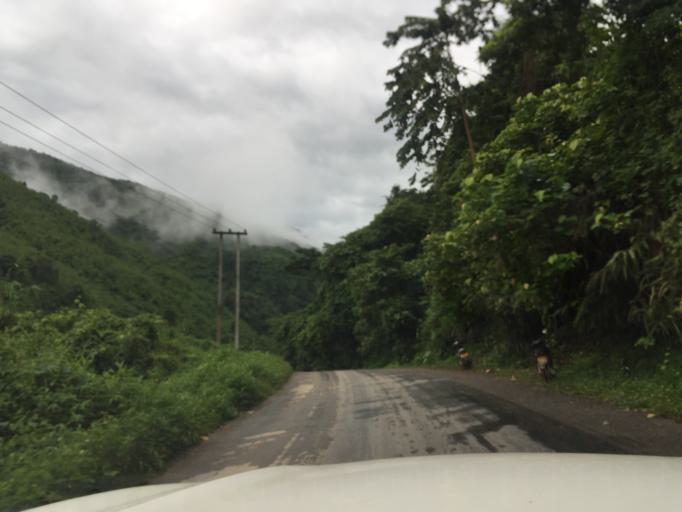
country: LA
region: Oudomxai
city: Muang La
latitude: 21.0446
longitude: 102.2410
